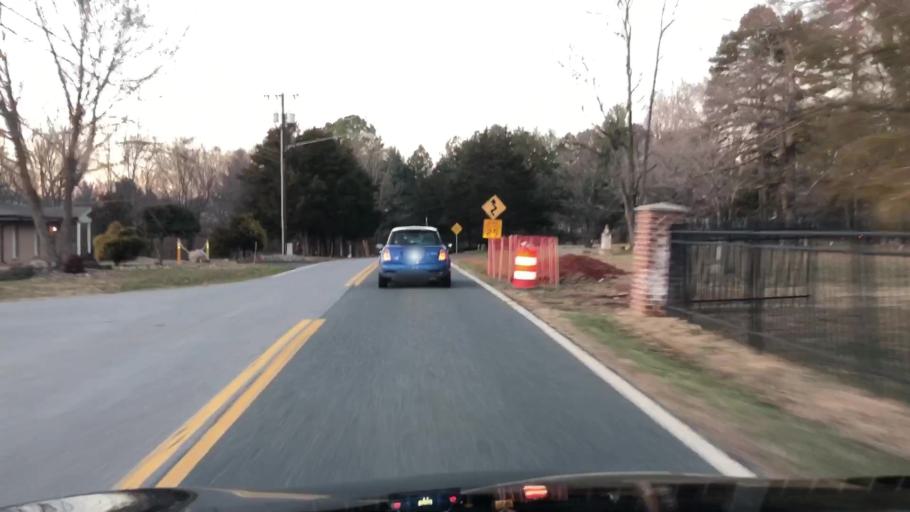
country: US
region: Virginia
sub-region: City of Lynchburg
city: West Lynchburg
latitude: 37.4103
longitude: -79.2243
